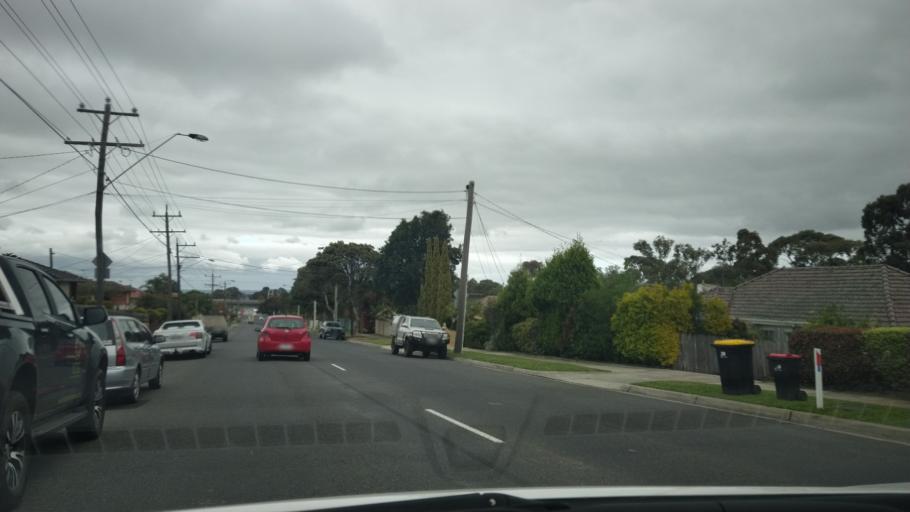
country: AU
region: Victoria
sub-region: Greater Dandenong
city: Dandenong
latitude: -37.9701
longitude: 145.1865
